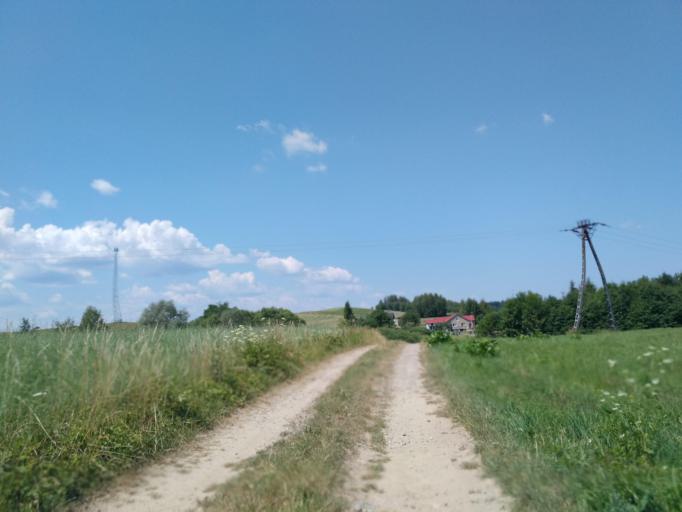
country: PL
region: Subcarpathian Voivodeship
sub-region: Powiat sanocki
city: Poraz
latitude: 49.4768
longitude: 22.1930
